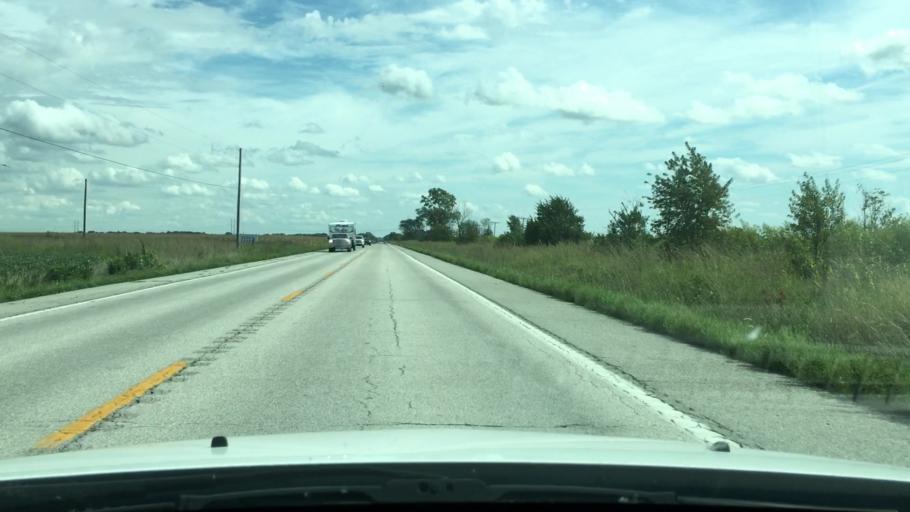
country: US
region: Missouri
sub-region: Audrain County
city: Vandalia
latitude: 39.2856
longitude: -91.5444
